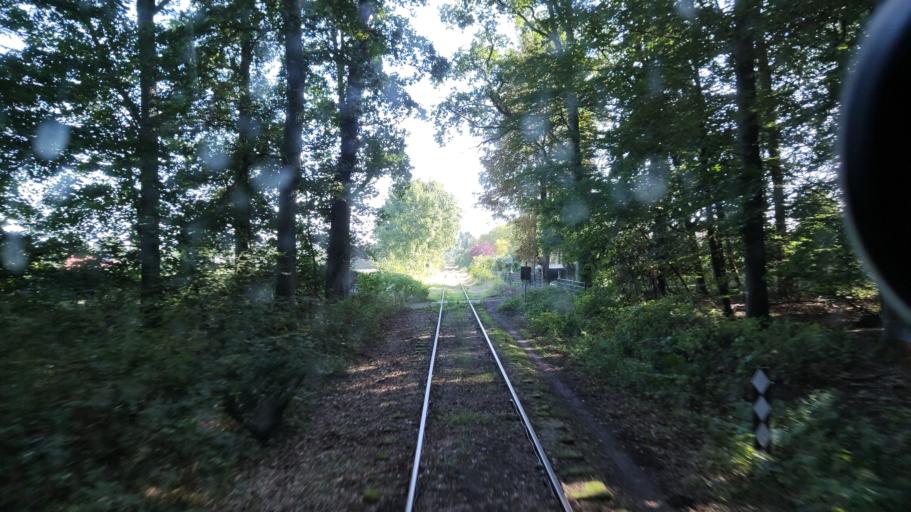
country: DE
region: Lower Saxony
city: Adendorf
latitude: 53.2606
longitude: 10.4570
